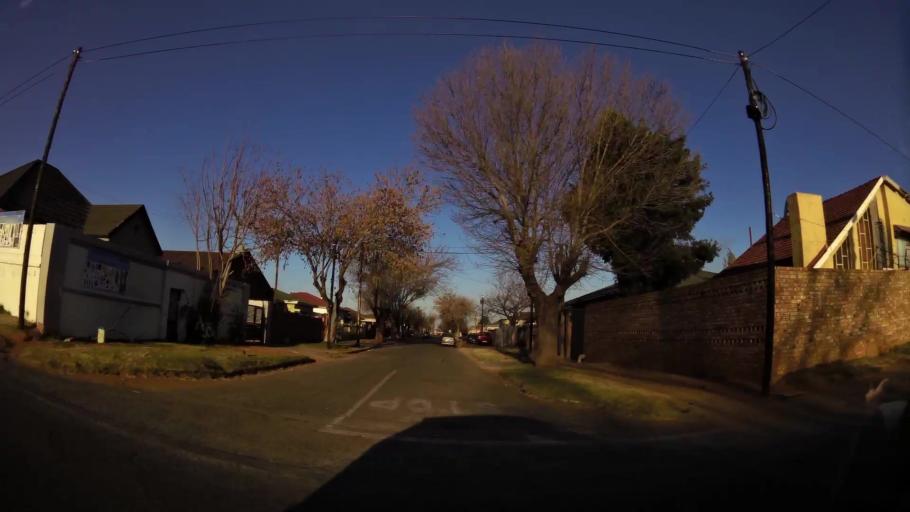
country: ZA
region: Gauteng
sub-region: City of Johannesburg Metropolitan Municipality
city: Roodepoort
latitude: -26.1619
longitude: 27.8730
